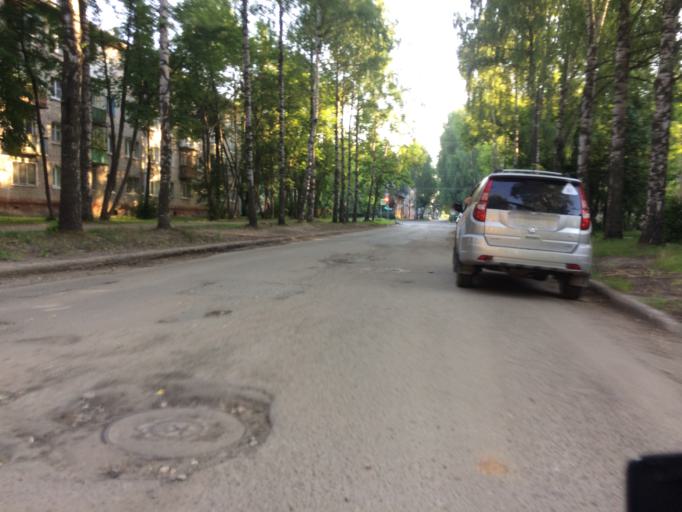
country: RU
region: Mariy-El
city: Yoshkar-Ola
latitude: 56.6468
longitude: 47.8818
